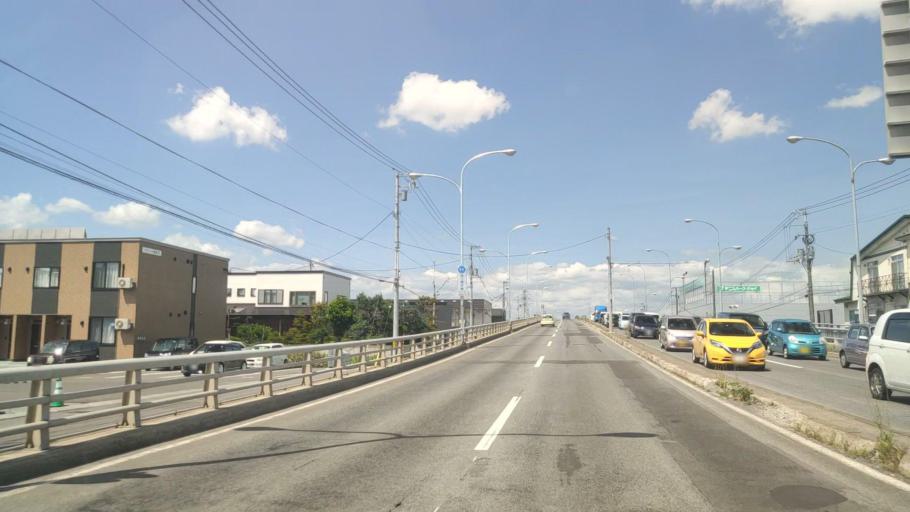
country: JP
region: Hokkaido
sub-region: Asahikawa-shi
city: Asahikawa
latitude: 43.7920
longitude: 142.4032
